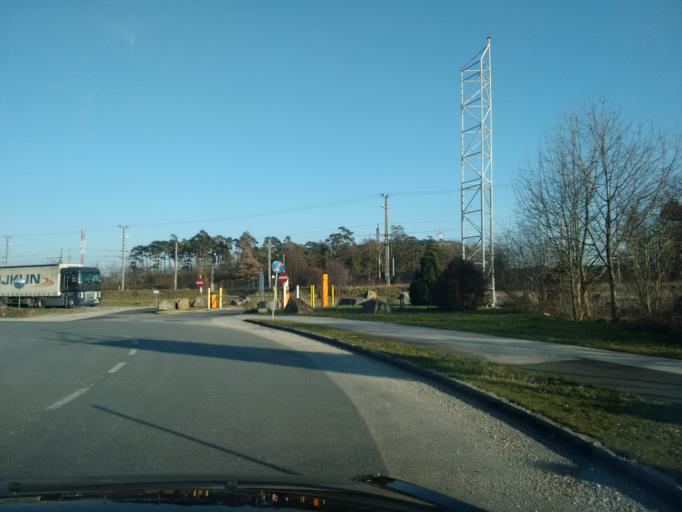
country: AT
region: Upper Austria
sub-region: Wels-Land
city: Holzhausen
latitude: 48.1893
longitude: 14.0747
